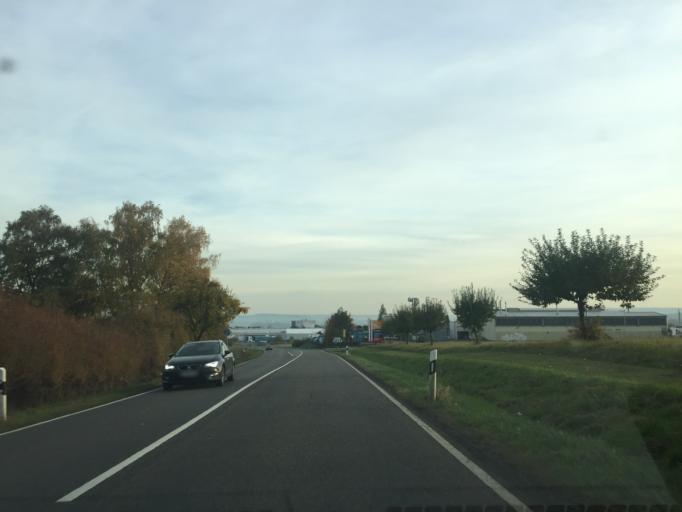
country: DE
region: Hesse
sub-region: Regierungsbezirk Giessen
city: Elz
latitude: 50.4272
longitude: 8.0170
